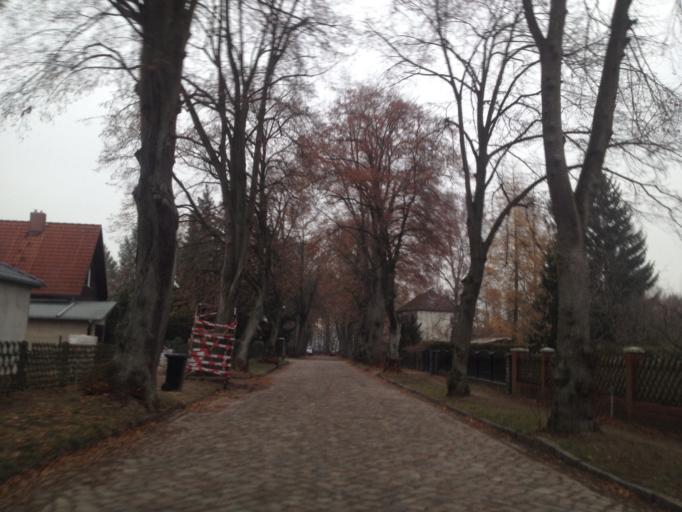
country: DE
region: Berlin
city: Blankenfelde
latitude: 52.6885
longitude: 13.3743
